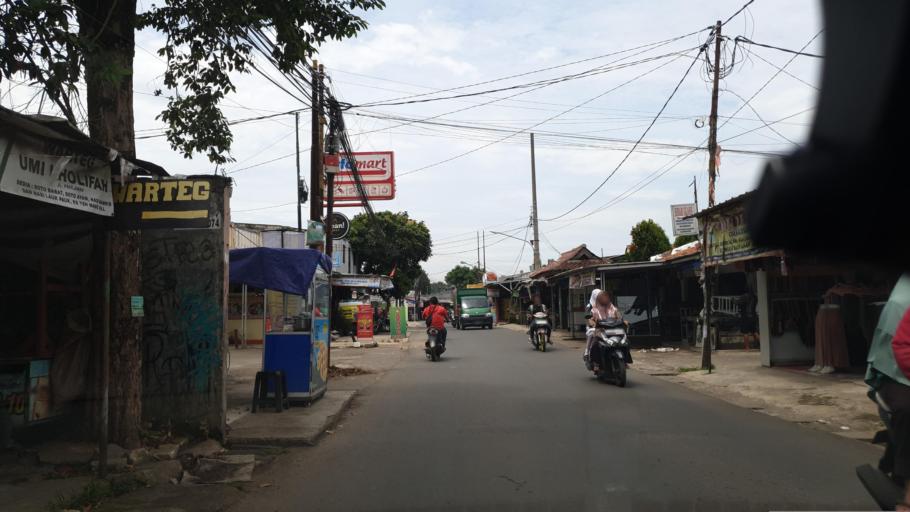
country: ID
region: West Java
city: Pamulang
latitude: -6.3677
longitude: 106.7550
